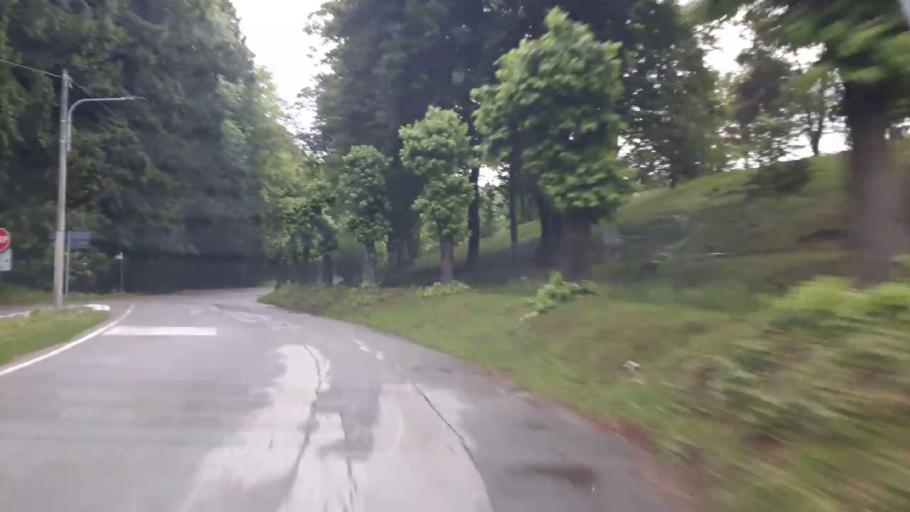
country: IT
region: Piedmont
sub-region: Provincia Verbano-Cusio-Ossola
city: Gignese
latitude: 45.8697
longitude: 8.5063
